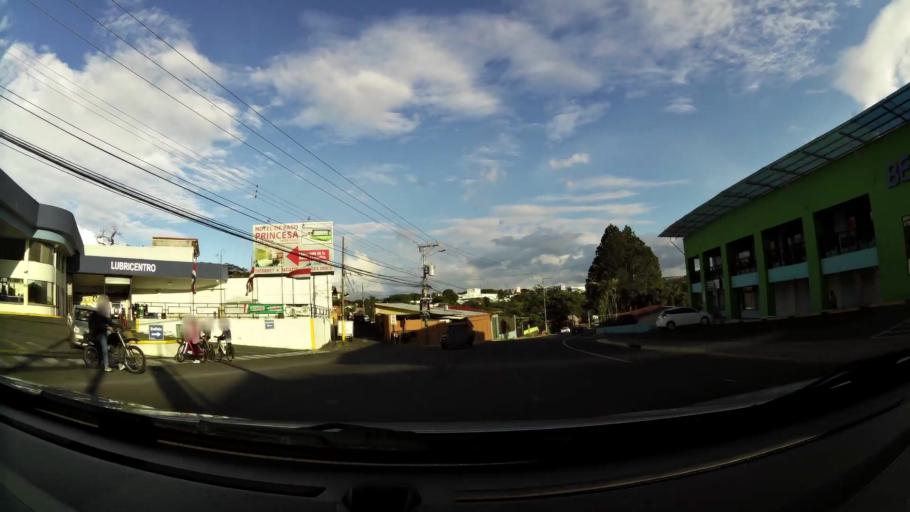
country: CR
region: Heredia
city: Llorente
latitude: 10.0068
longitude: -84.1762
